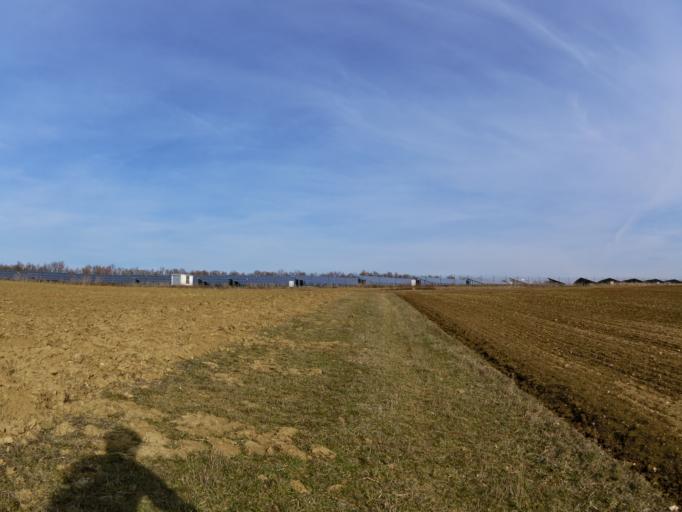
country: DE
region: Bavaria
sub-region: Regierungsbezirk Unterfranken
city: Kurnach
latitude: 49.8368
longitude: 10.0280
